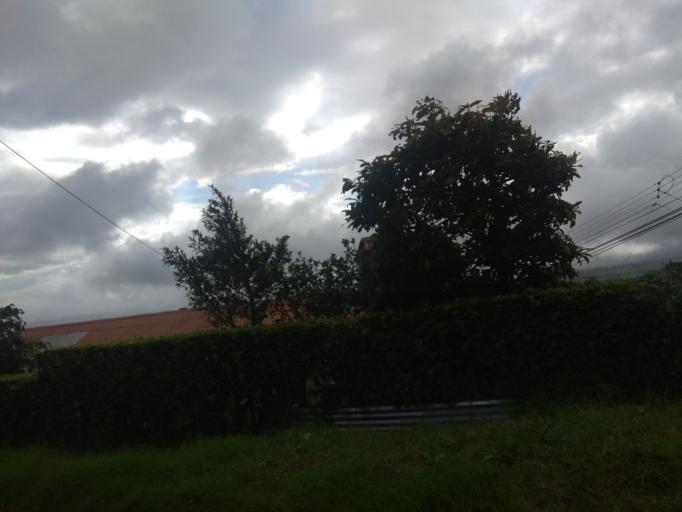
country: CR
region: San Jose
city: Ipis
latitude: 9.9865
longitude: -83.9595
